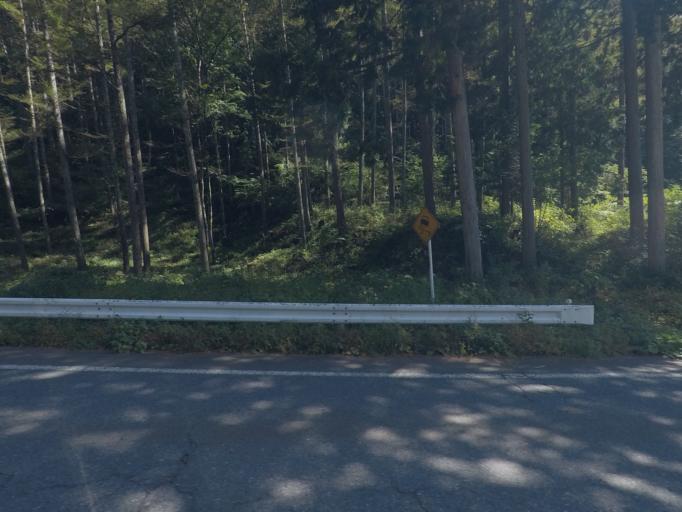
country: JP
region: Nagano
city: Shiojiri
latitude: 35.9946
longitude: 137.7393
